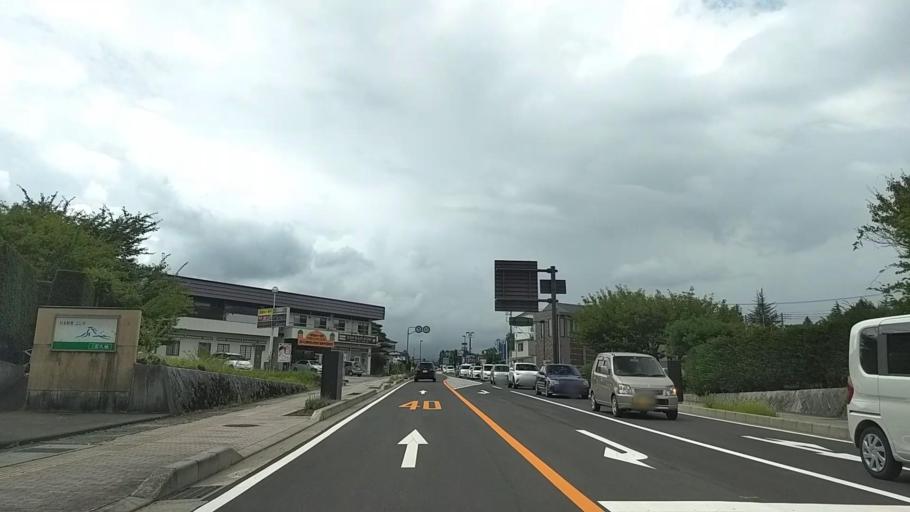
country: JP
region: Yamanashi
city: Fujikawaguchiko
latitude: 35.5054
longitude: 138.7593
